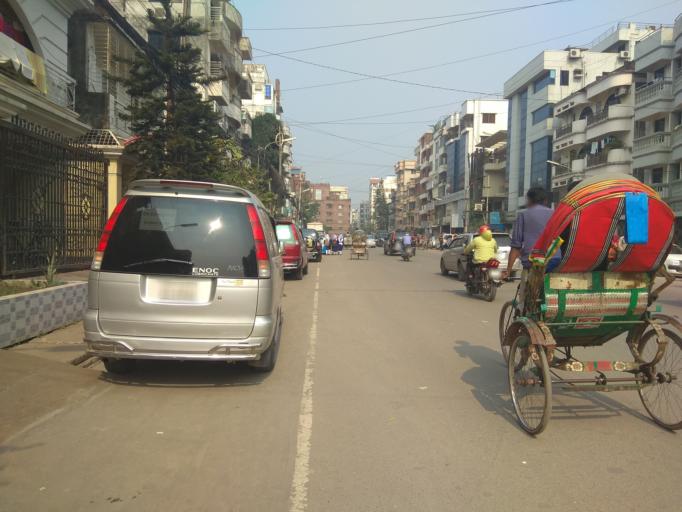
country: BD
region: Dhaka
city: Tungi
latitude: 23.8681
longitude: 90.3937
